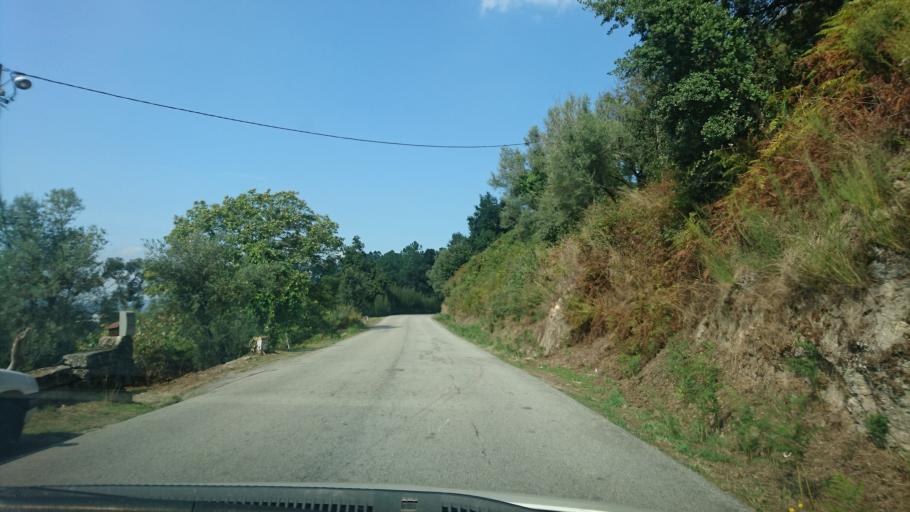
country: PT
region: Vila Real
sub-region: Mondim de Basto
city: Mondim de Basto
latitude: 41.4517
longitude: -7.9233
